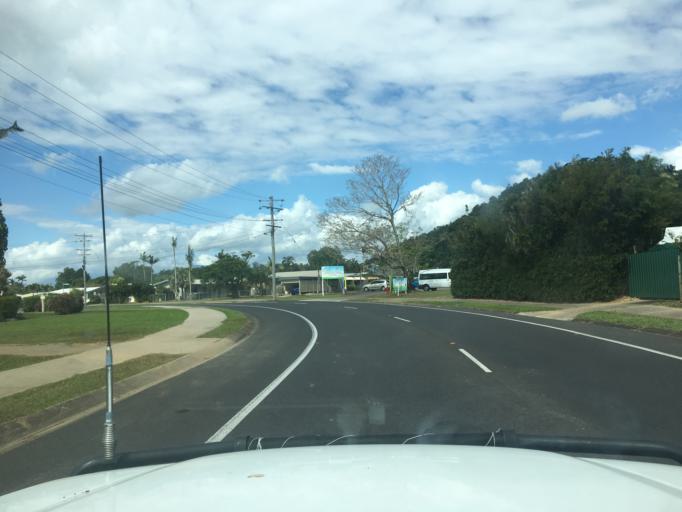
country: AU
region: Queensland
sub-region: Cairns
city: Woree
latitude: -16.9645
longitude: 145.7399
